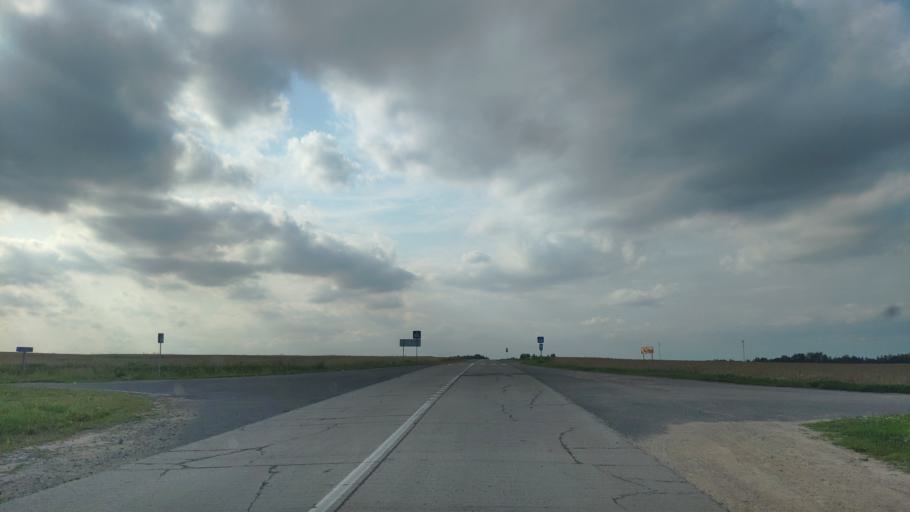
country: BY
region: Minsk
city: Khatsyezhyna
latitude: 53.8469
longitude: 27.2815
